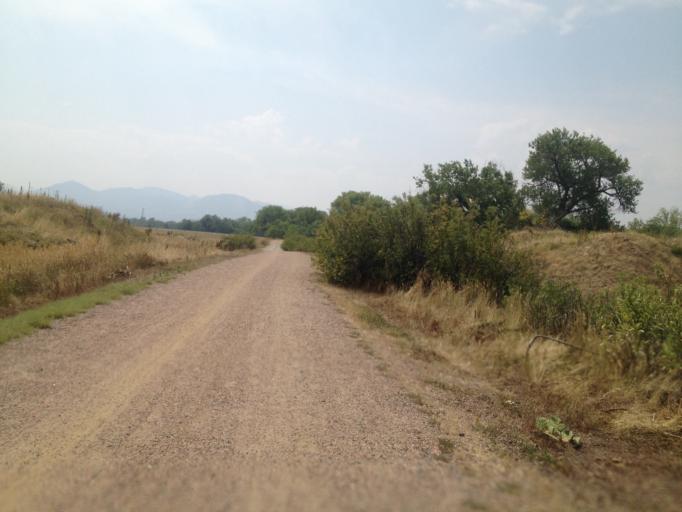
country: US
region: Colorado
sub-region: Boulder County
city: Superior
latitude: 39.9487
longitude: -105.1714
